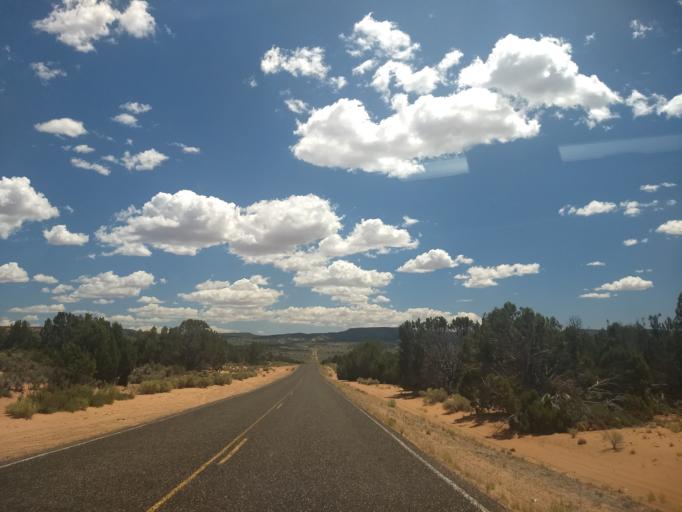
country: US
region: Utah
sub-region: Kane County
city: Kanab
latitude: 37.1758
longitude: -112.6598
